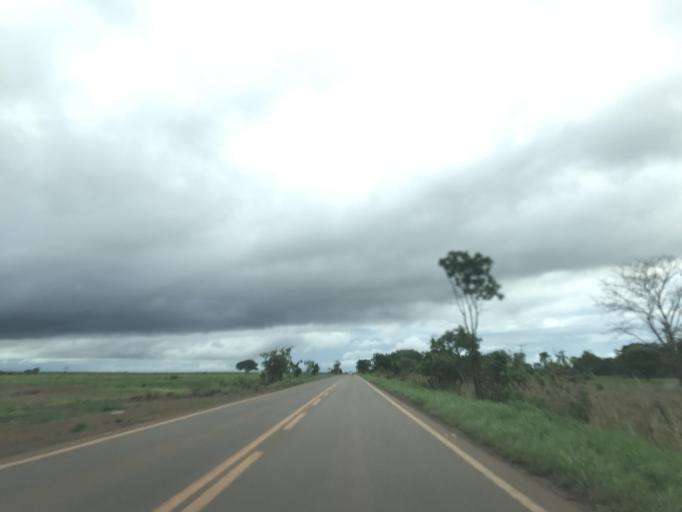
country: BR
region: Goias
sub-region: Luziania
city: Luziania
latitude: -16.4739
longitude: -48.2111
